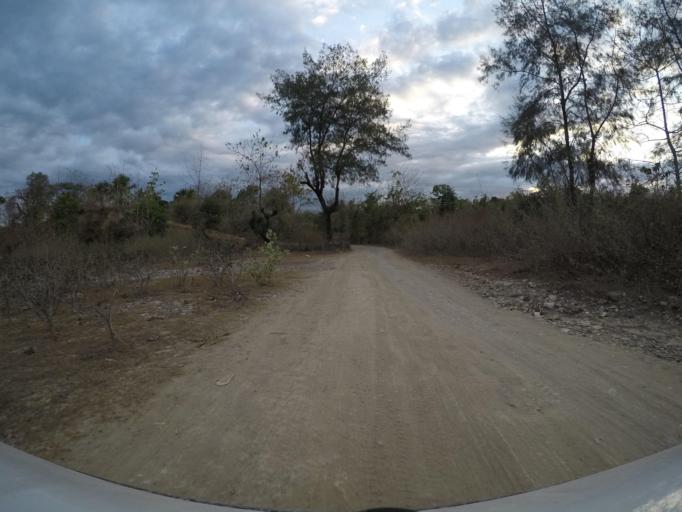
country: TL
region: Bobonaro
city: Maliana
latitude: -8.9136
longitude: 125.2153
